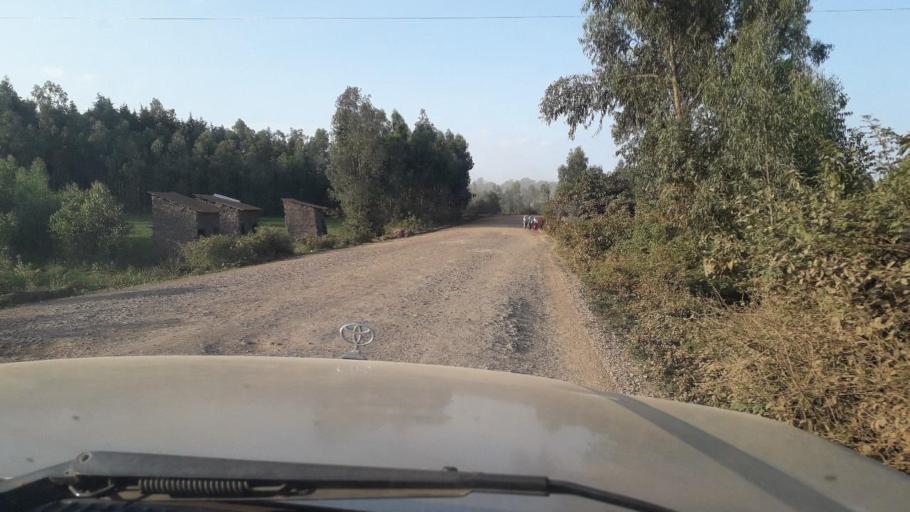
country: ET
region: Oromiya
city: Jima
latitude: 7.6171
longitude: 36.8342
